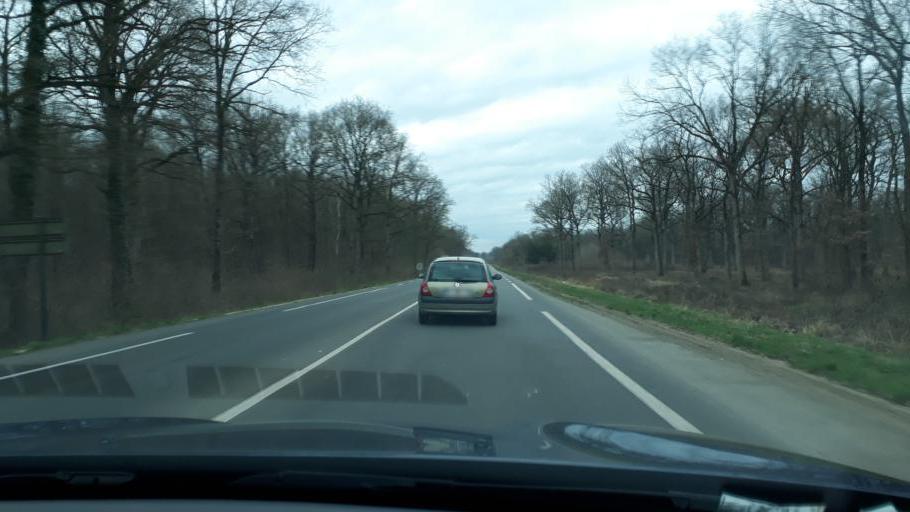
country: FR
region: Centre
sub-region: Departement du Loiret
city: Chanteau
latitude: 48.0084
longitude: 1.9538
